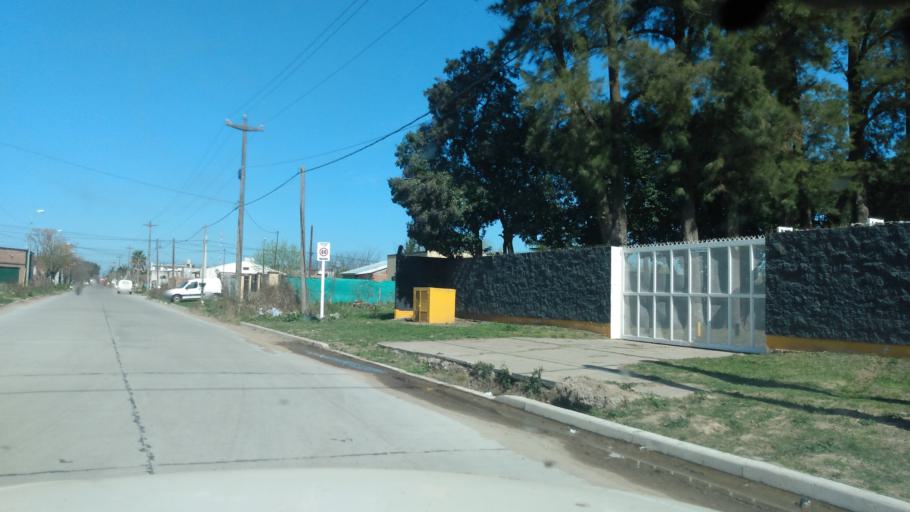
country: AR
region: Buenos Aires
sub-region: Partido de Lujan
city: Lujan
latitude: -34.5771
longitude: -59.1274
